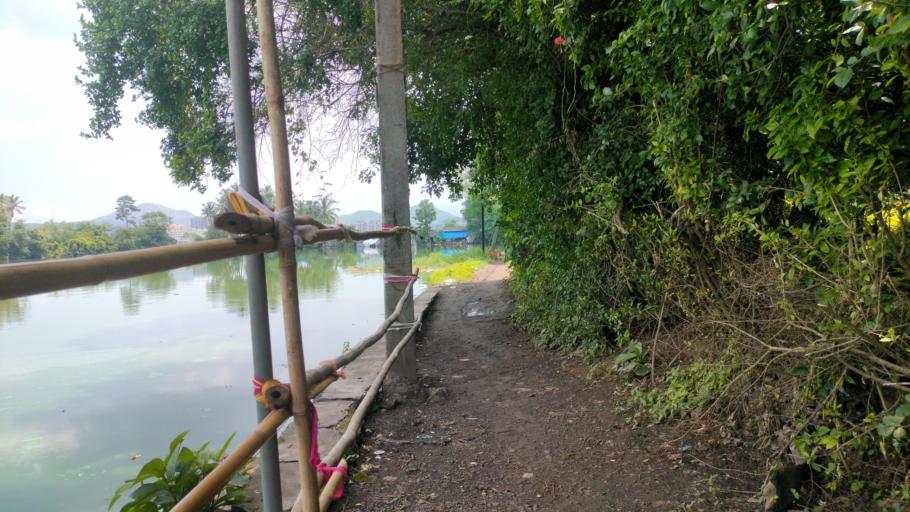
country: IN
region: Maharashtra
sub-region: Thane
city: Virar
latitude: 19.4230
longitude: 72.7985
